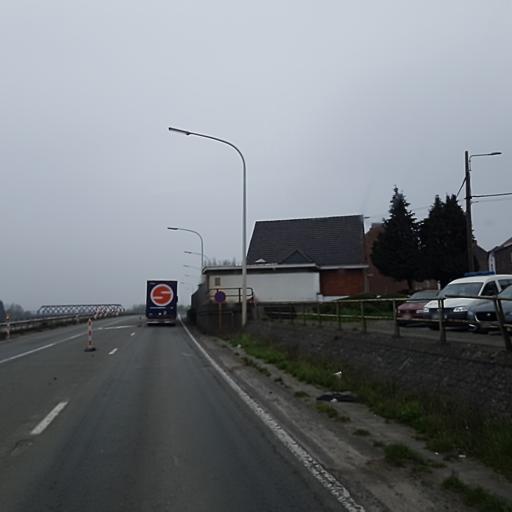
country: BE
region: Wallonia
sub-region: Province du Hainaut
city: Mons
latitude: 50.4784
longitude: 3.9490
